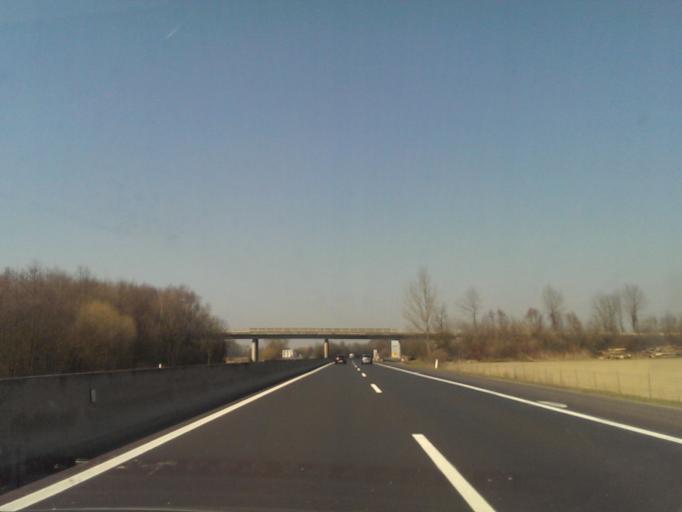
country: AT
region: Upper Austria
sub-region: Politischer Bezirk Scharding
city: Sankt Marienkirchen bei Schaerding
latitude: 48.3292
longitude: 13.4111
